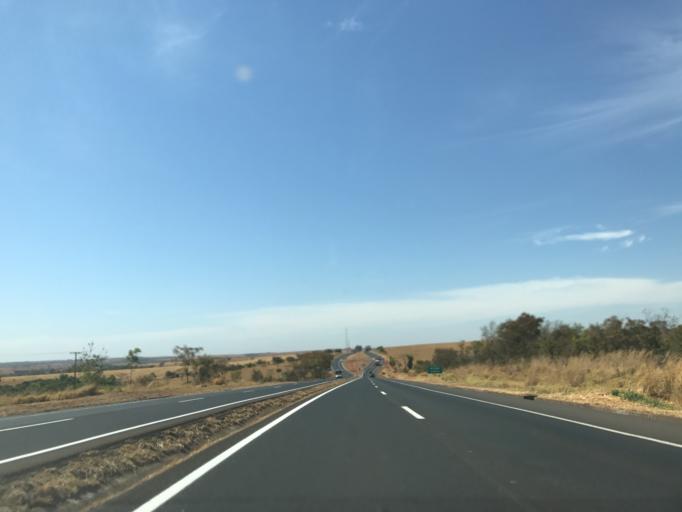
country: BR
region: Minas Gerais
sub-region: Monte Alegre De Minas
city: Monte Alegre de Minas
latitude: -18.8522
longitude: -49.0839
